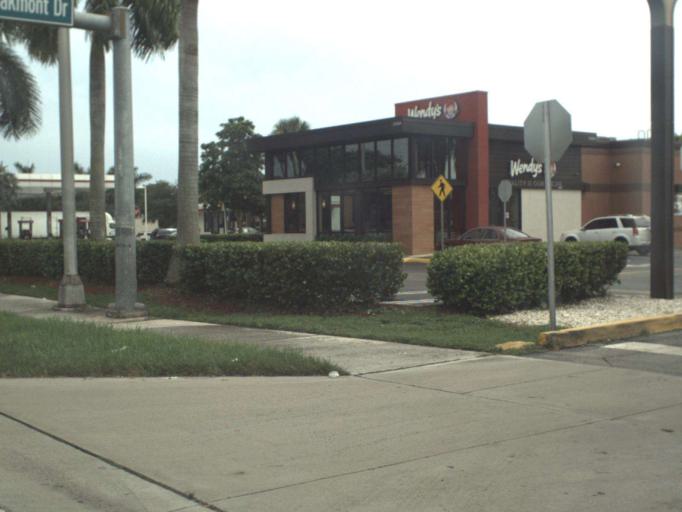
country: US
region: Florida
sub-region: Miami-Dade County
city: Country Club
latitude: 25.9423
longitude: -80.3237
